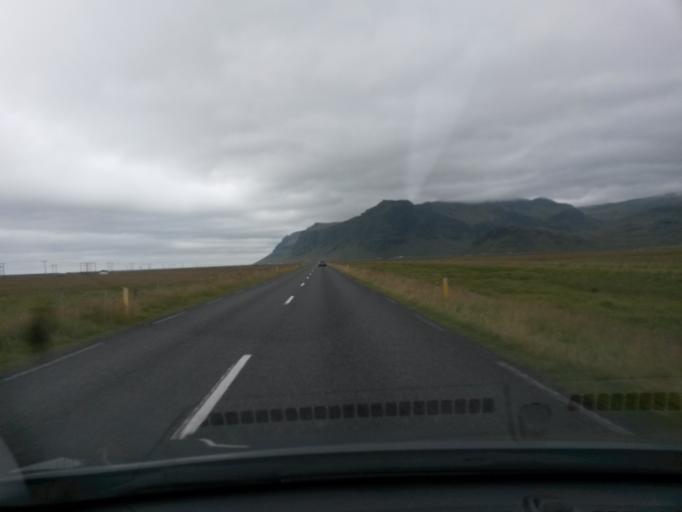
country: IS
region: South
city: Vestmannaeyjar
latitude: 63.5245
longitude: -19.5857
